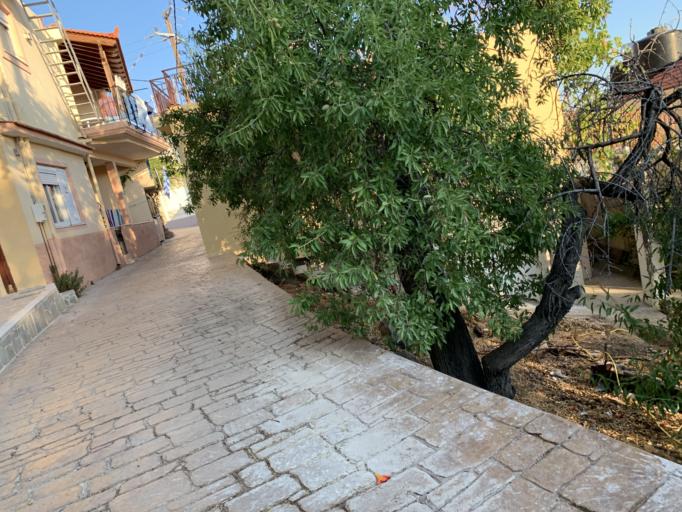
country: GR
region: North Aegean
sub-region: Chios
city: Vrontados
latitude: 38.5272
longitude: 25.8674
